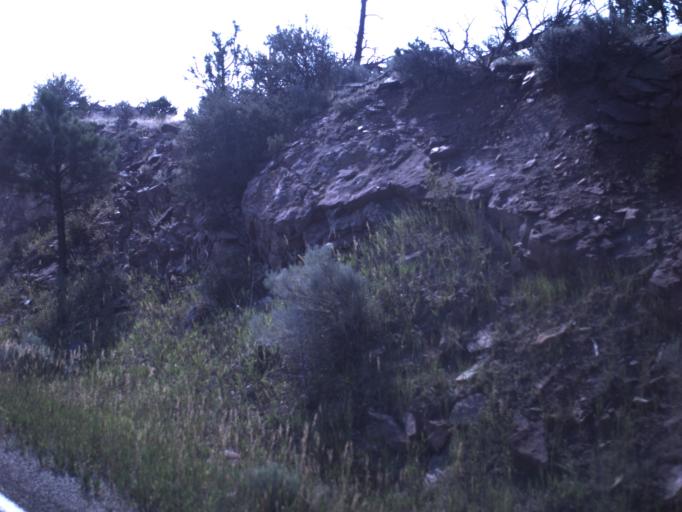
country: US
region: Utah
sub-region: Daggett County
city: Manila
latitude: 40.9418
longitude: -109.4185
